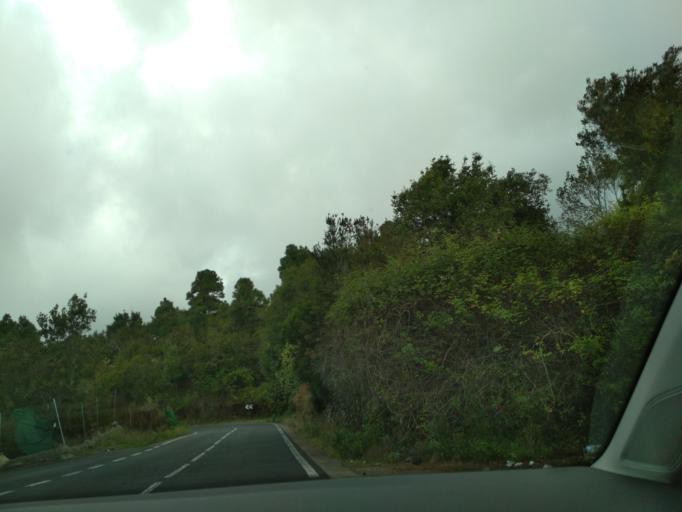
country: ES
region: Canary Islands
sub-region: Provincia de Santa Cruz de Tenerife
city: Garachico
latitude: 28.3463
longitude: -16.7512
